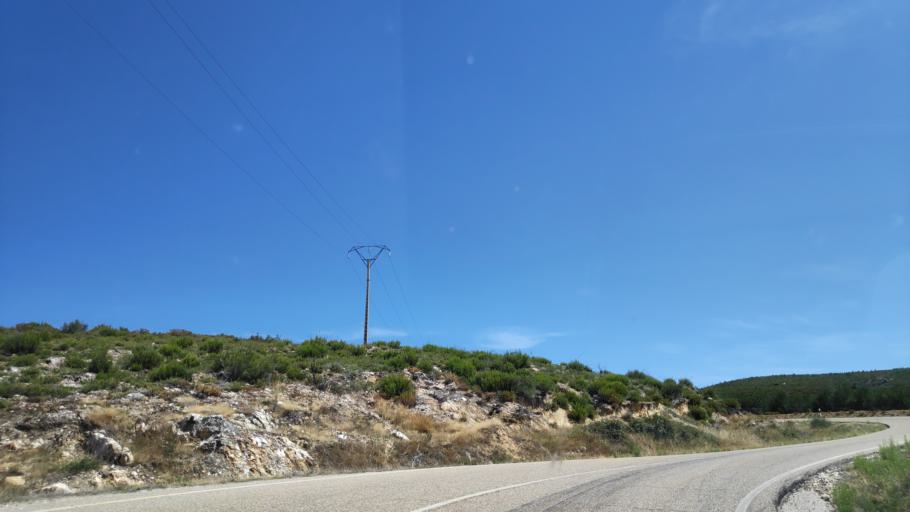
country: ES
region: Castille and Leon
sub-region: Provincia de Zamora
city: Requejo
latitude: 42.0070
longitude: -6.6960
